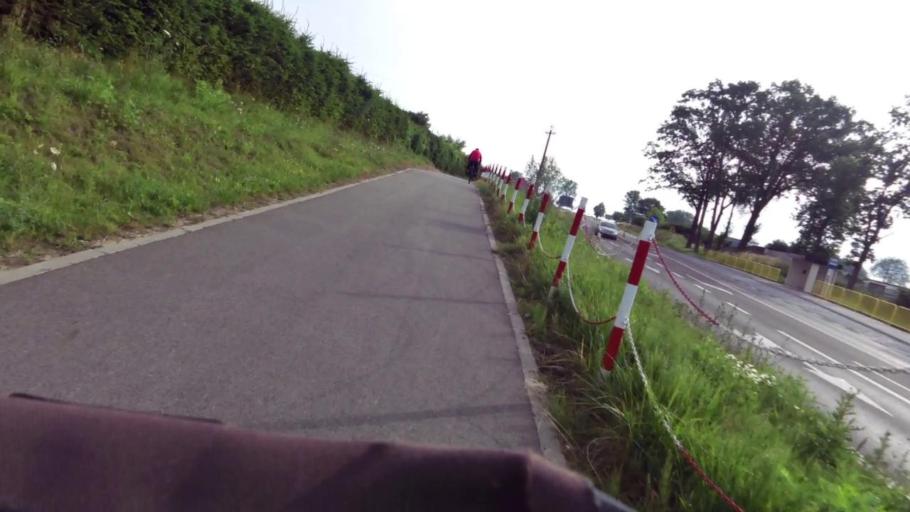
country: PL
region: West Pomeranian Voivodeship
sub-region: Powiat kamienski
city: Kamien Pomorski
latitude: 53.9778
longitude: 14.7913
